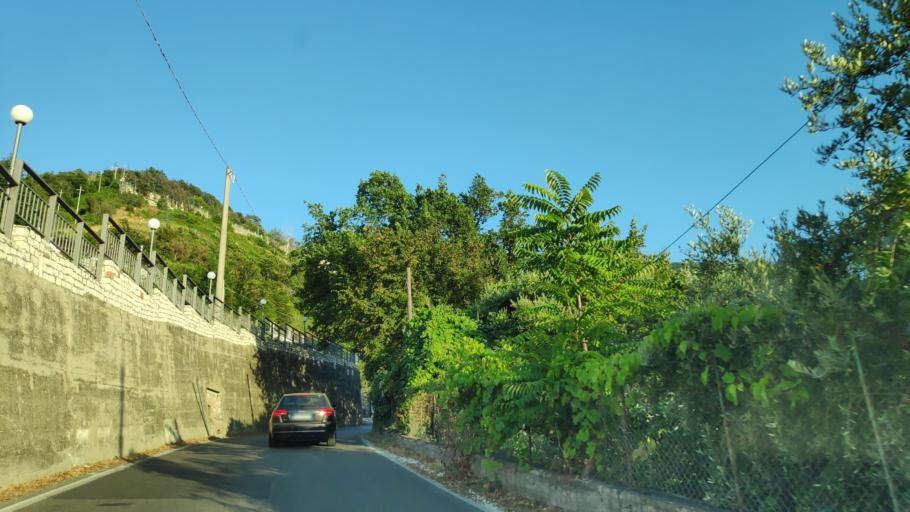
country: IT
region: Campania
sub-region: Provincia di Salerno
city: Corbara
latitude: 40.7263
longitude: 14.5984
